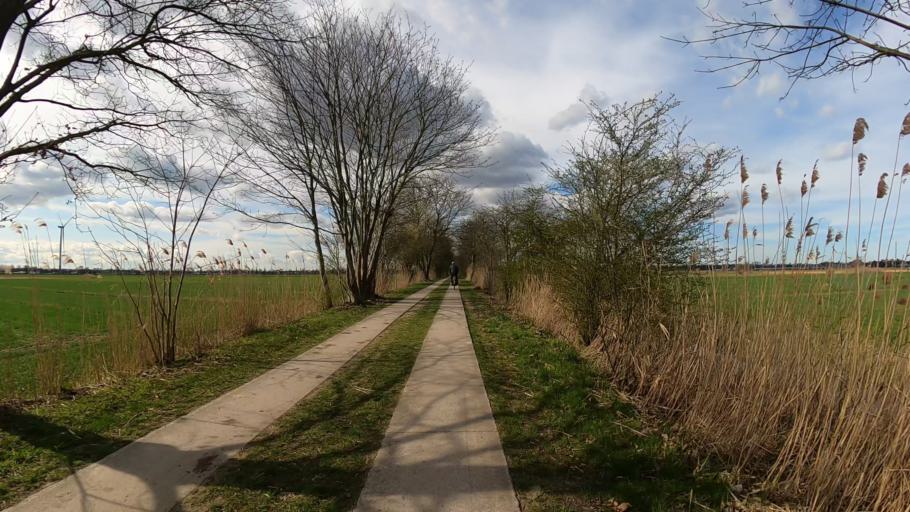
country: DE
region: Lower Saxony
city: Stelle
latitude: 53.4654
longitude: 10.0987
